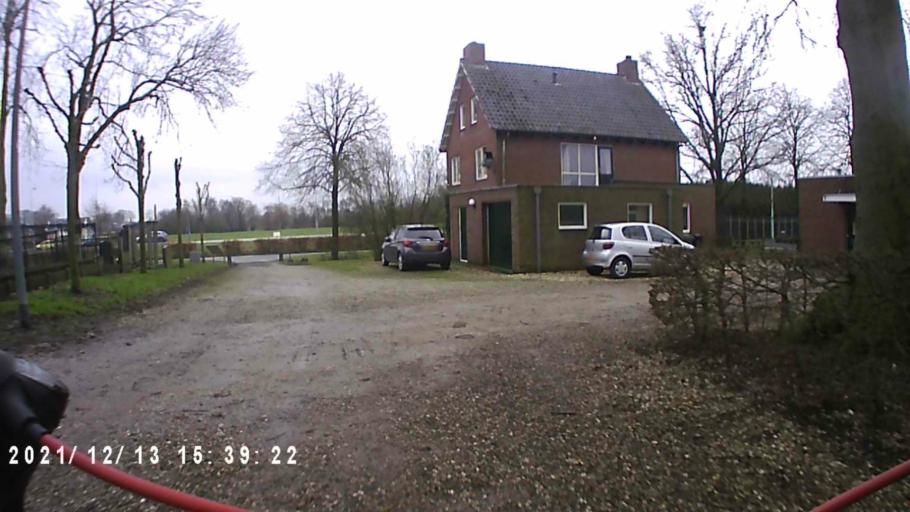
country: NL
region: Groningen
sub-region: Gemeente Appingedam
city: Appingedam
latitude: 53.3232
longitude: 6.8335
